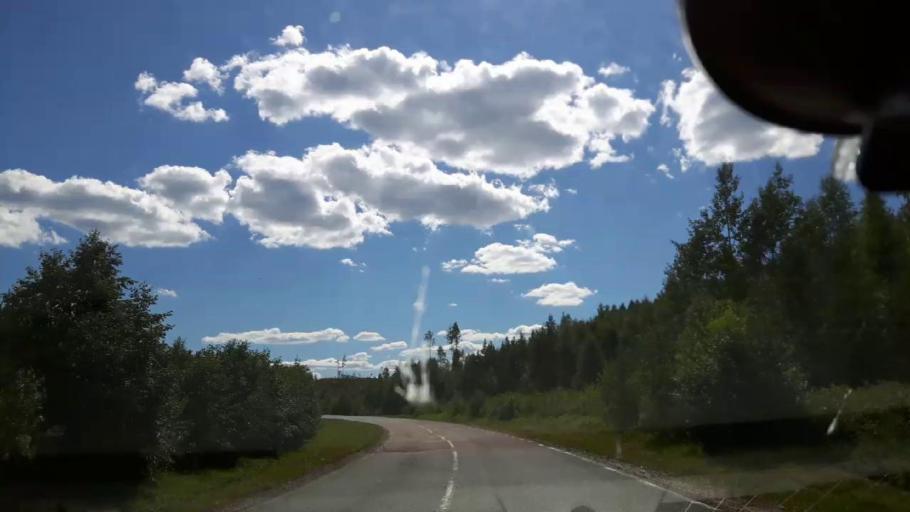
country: SE
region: Jaemtland
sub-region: Ragunda Kommun
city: Hammarstrand
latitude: 62.8678
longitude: 16.2142
